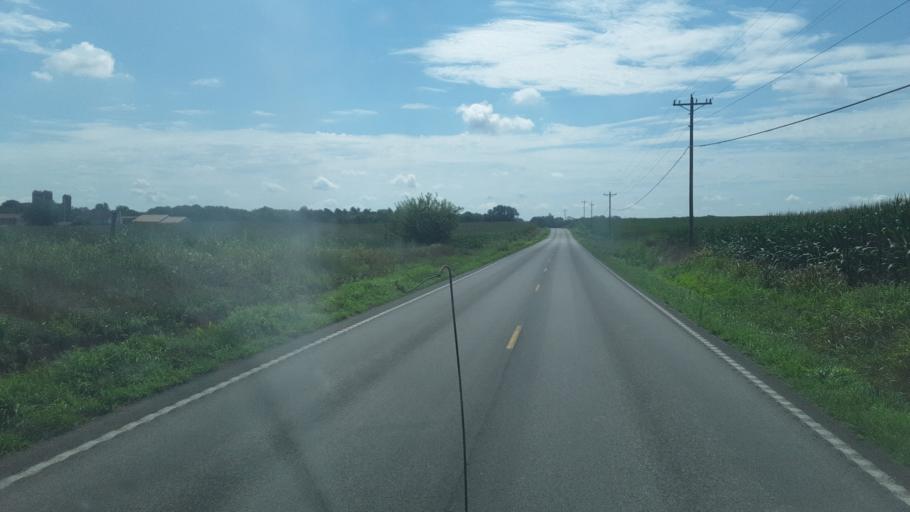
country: US
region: Kentucky
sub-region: Christian County
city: Oak Grove
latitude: 36.7722
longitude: -87.3413
